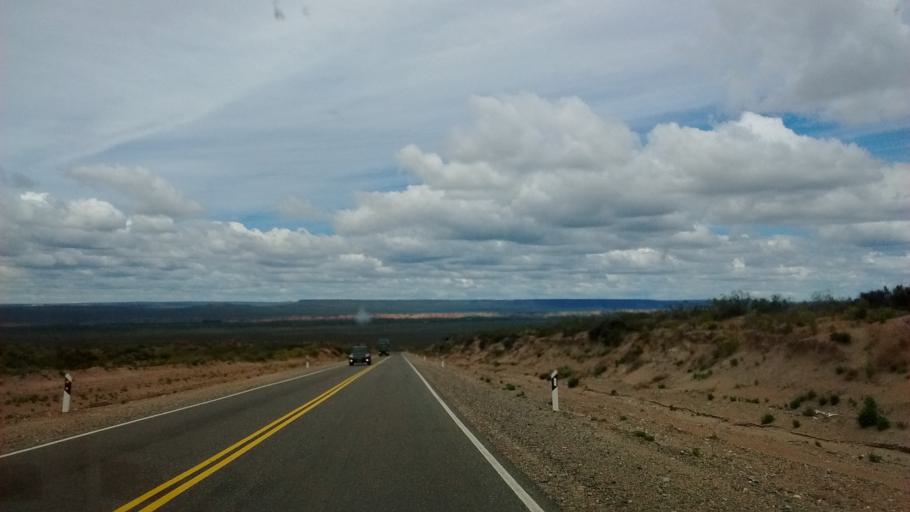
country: AR
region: Neuquen
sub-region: Departamento de Picun Leufu
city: Picun Leufu
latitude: -39.7713
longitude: -69.6523
